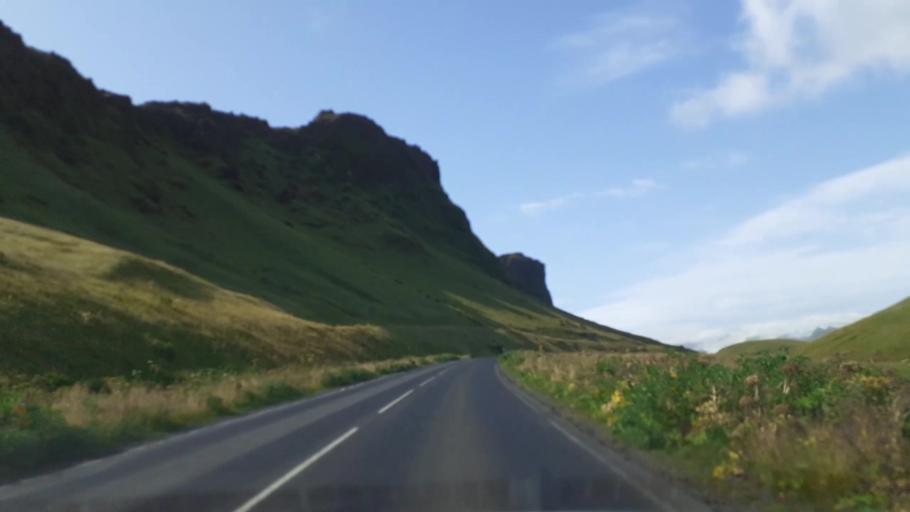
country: IS
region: South
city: Vestmannaeyjar
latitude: 63.4237
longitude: -19.0183
